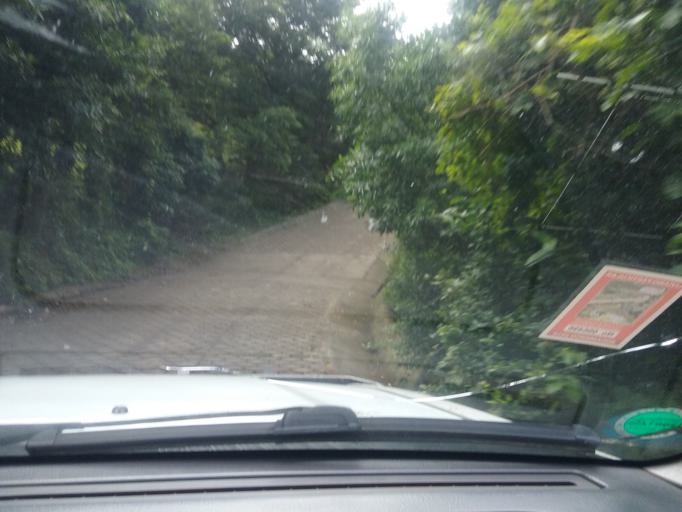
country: NI
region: Matagalpa
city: Matagalpa
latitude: 12.8725
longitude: -85.9452
